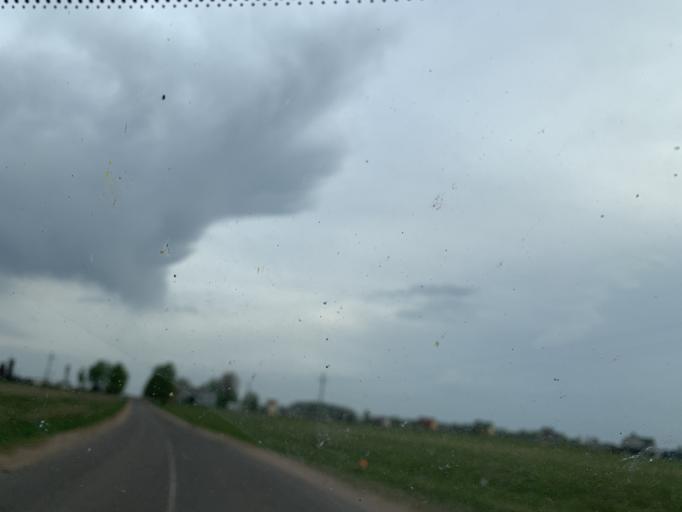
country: BY
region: Minsk
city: Kapyl'
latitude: 53.2669
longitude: 26.9571
